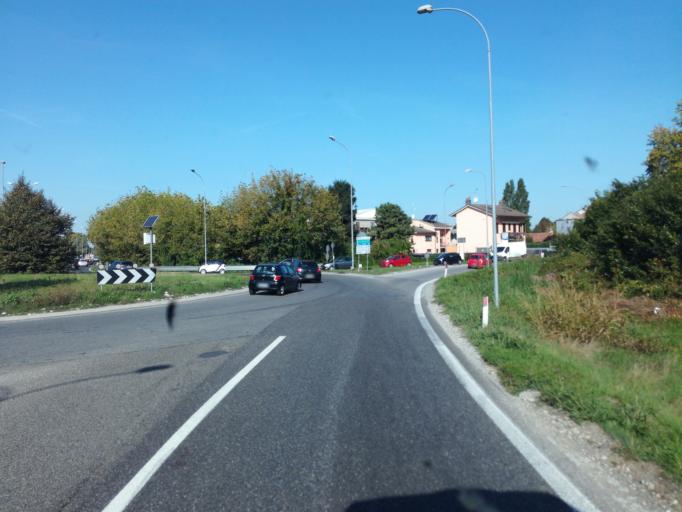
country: IT
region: Lombardy
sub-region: Provincia di Lodi
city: Lodi
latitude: 45.2972
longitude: 9.5033
